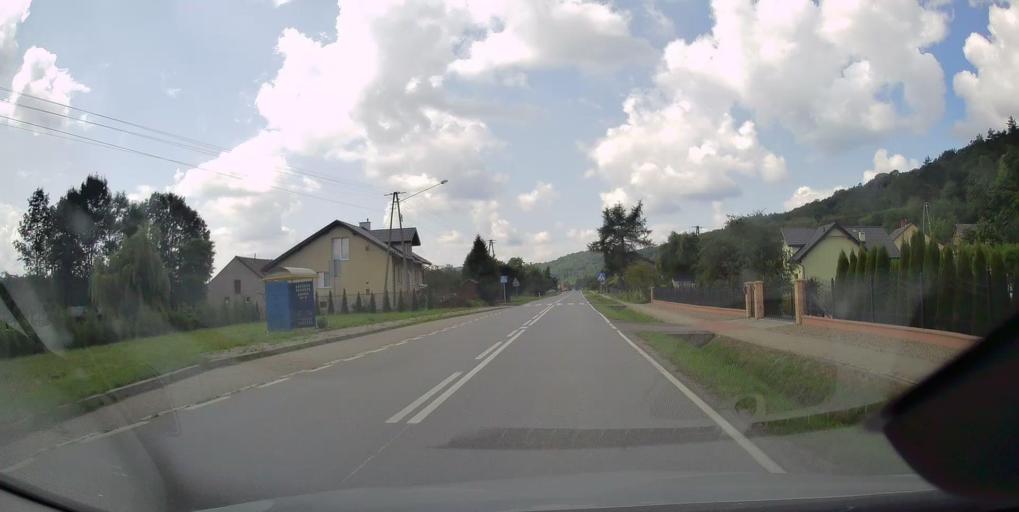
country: PL
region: Lesser Poland Voivodeship
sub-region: Powiat tarnowski
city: Wielka Wies
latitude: 49.9223
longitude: 20.8286
